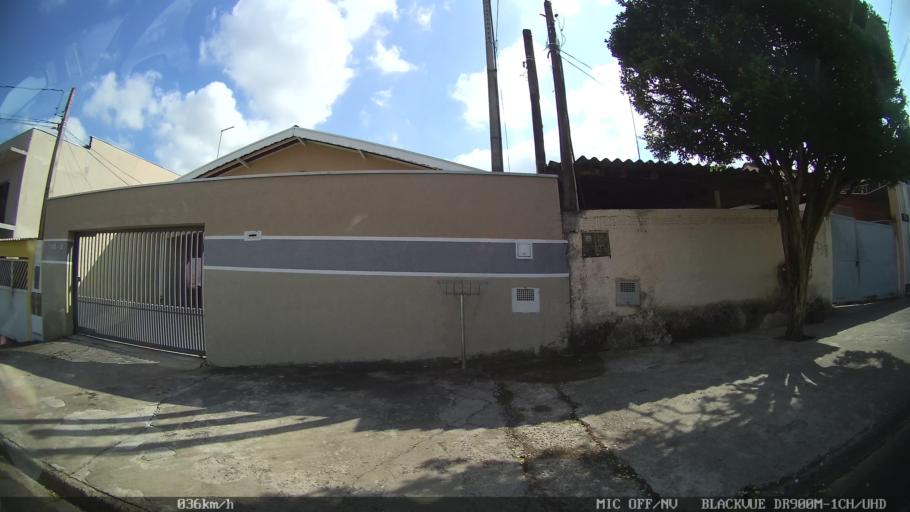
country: BR
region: Sao Paulo
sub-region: Campinas
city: Campinas
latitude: -22.9384
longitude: -47.1179
